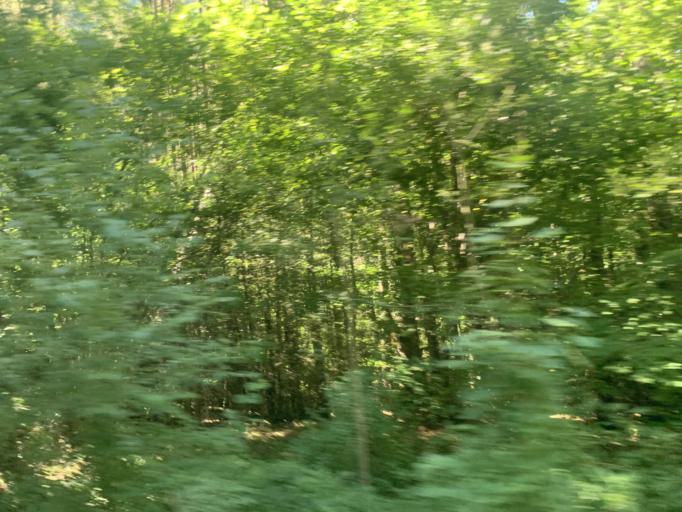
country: ES
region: Aragon
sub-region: Provincia de Huesca
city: Broto
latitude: 42.6543
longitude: -0.0939
